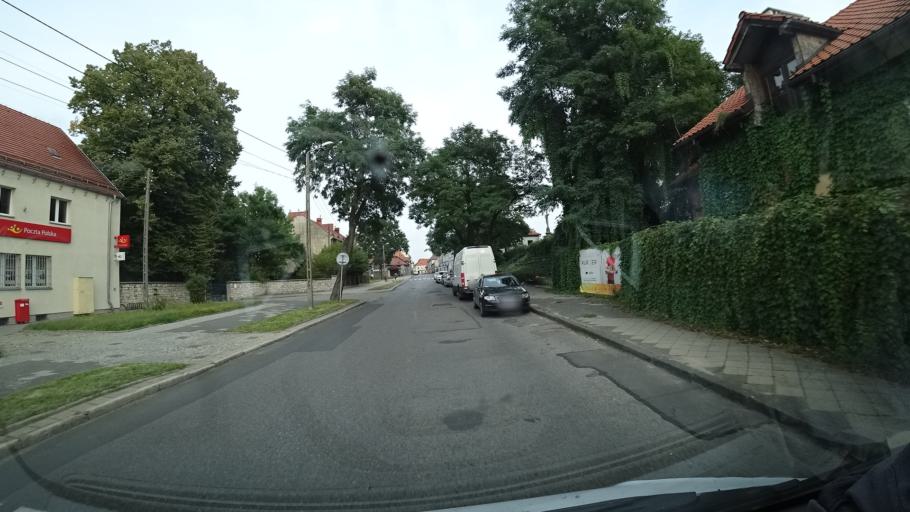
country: PL
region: Silesian Voivodeship
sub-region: Powiat gliwicki
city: Pyskowice
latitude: 50.3980
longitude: 18.6236
